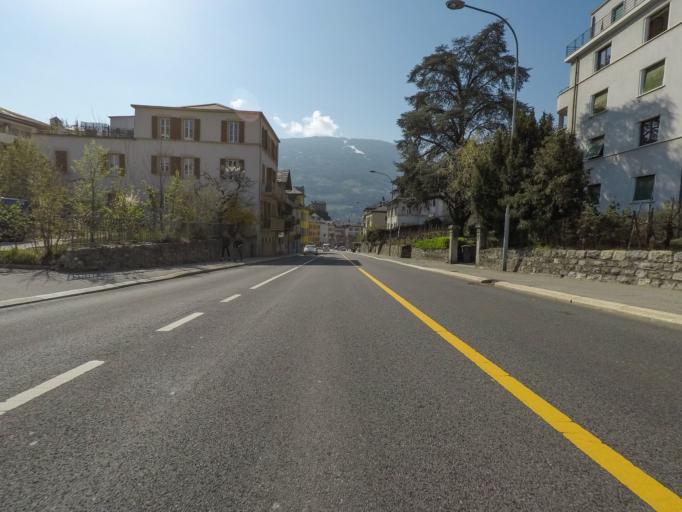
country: CH
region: Valais
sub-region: Sion District
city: Sitten
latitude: 46.2371
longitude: 7.3603
